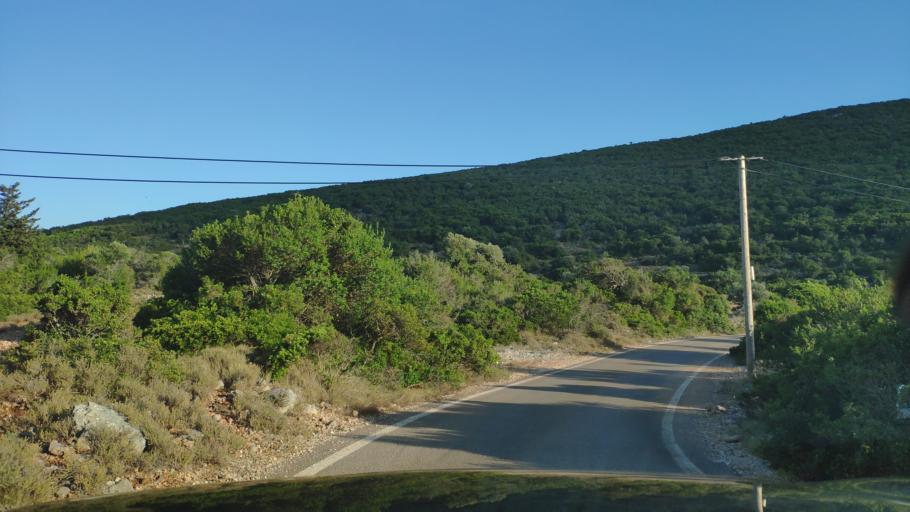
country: GR
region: Ionian Islands
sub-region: Lefkada
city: Nidri
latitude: 38.6092
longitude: 20.5669
